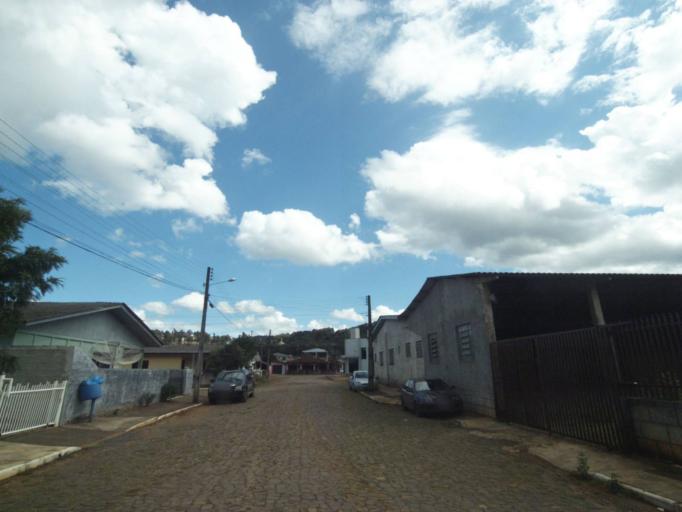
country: BR
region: Parana
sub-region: Uniao Da Vitoria
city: Uniao da Vitoria
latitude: -26.1497
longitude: -51.5435
